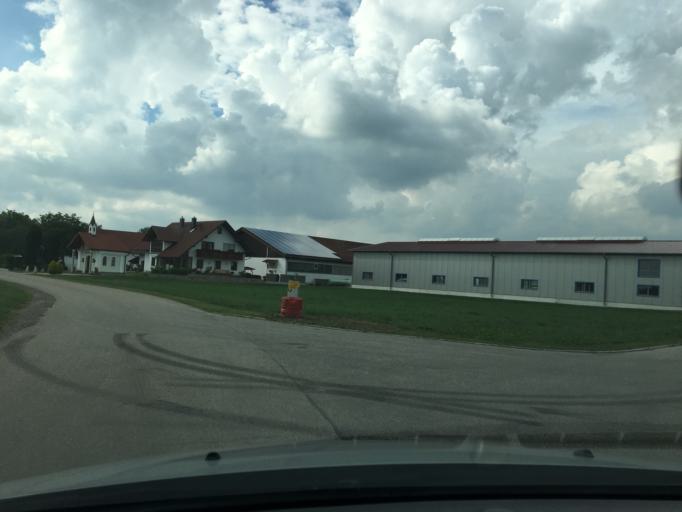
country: DE
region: Bavaria
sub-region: Lower Bavaria
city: Bruckberg
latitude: 48.4796
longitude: 12.0085
